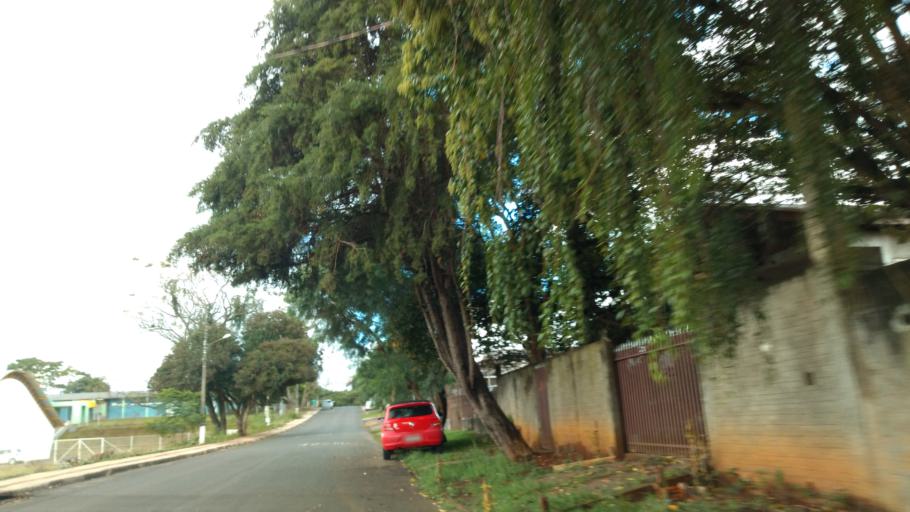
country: BR
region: Parana
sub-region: Guarapuava
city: Guarapuava
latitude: -25.3960
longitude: -51.4904
